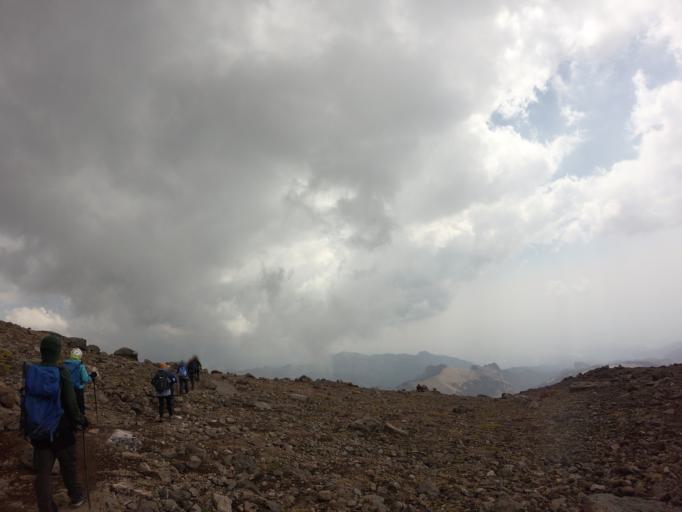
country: MX
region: Mexico
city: Amecameca de Juarez
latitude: 19.1617
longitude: -98.6455
